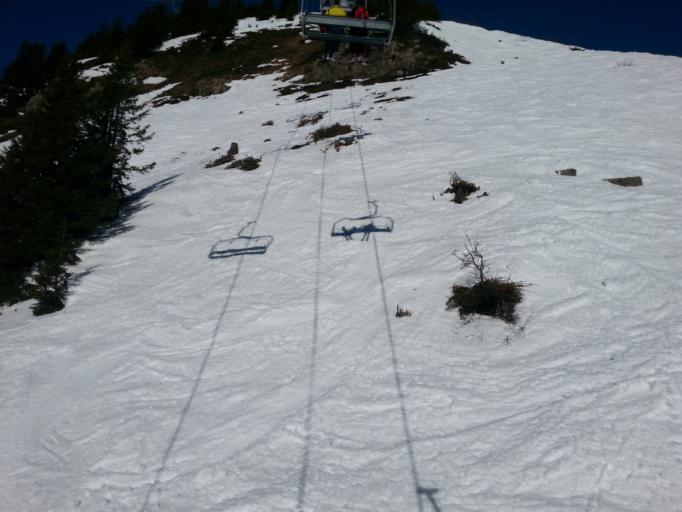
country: FR
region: Rhone-Alpes
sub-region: Departement de la Haute-Savoie
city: Samoens
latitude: 46.0264
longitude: 6.6963
